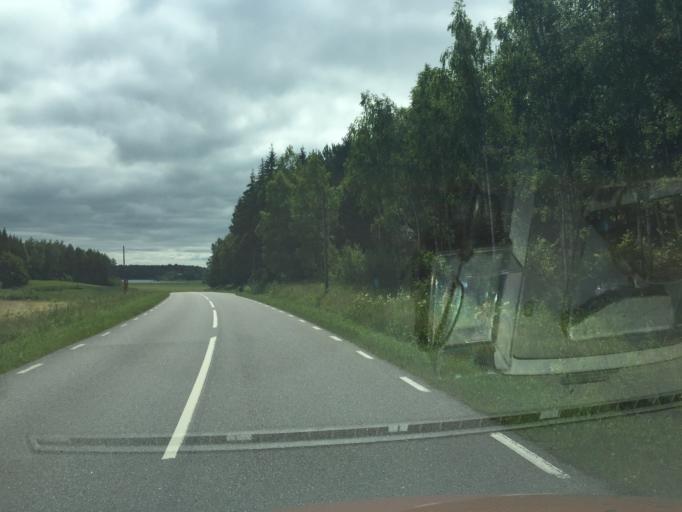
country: SE
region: Soedermanland
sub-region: Trosa Kommun
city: Trosa
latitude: 58.9739
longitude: 17.6930
